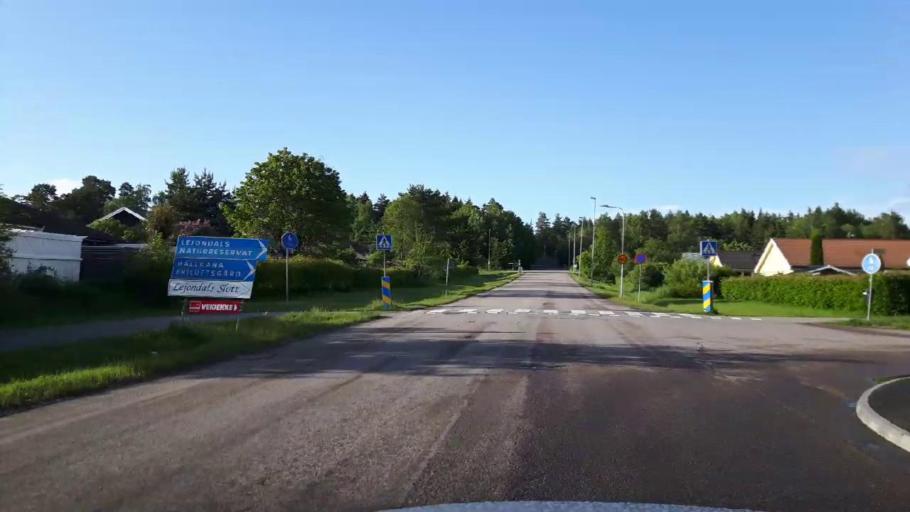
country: SE
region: Stockholm
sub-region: Upplands-Bro Kommun
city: Bro
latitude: 59.5188
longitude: 17.6581
